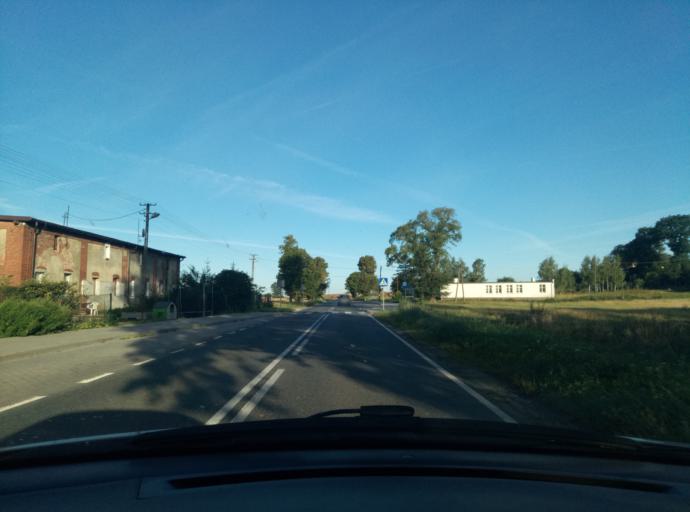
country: PL
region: Kujawsko-Pomorskie
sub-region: Powiat grudziadzki
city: Radzyn Chelminski
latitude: 53.3811
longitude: 18.9763
